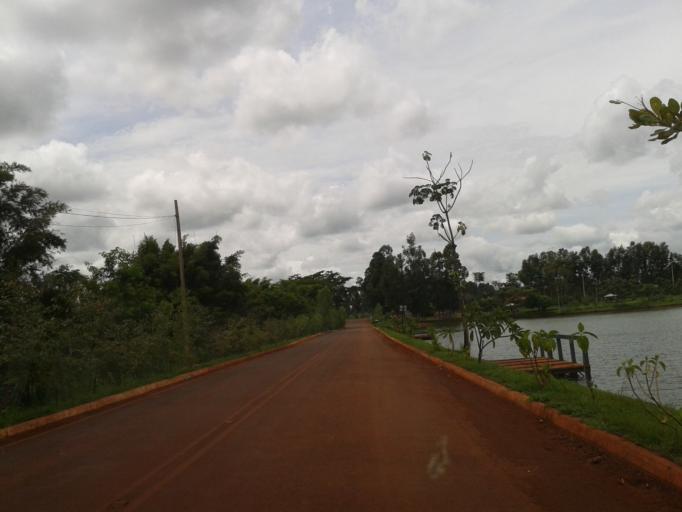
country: BR
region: Minas Gerais
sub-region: Centralina
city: Centralina
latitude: -18.5919
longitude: -49.2130
